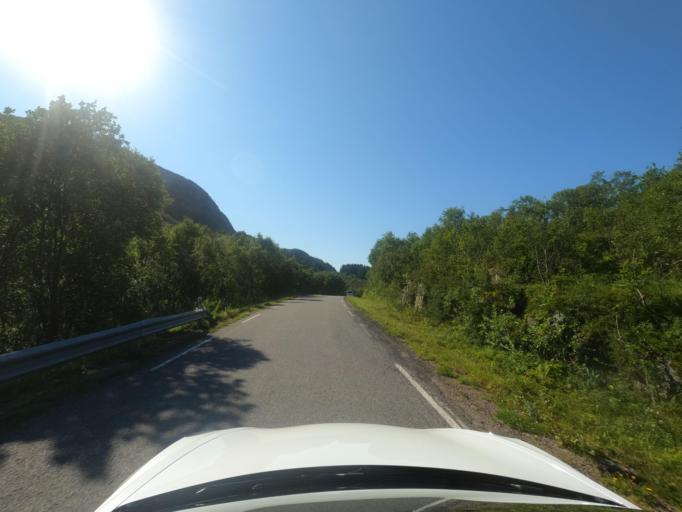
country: NO
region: Nordland
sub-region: Hadsel
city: Stokmarknes
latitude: 68.3215
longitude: 15.0050
